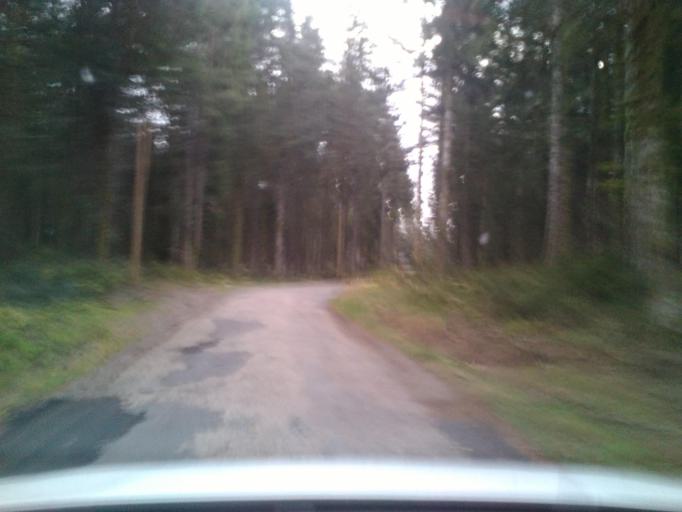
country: FR
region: Lorraine
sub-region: Departement des Vosges
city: Gerardmer
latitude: 48.0859
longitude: 6.8542
